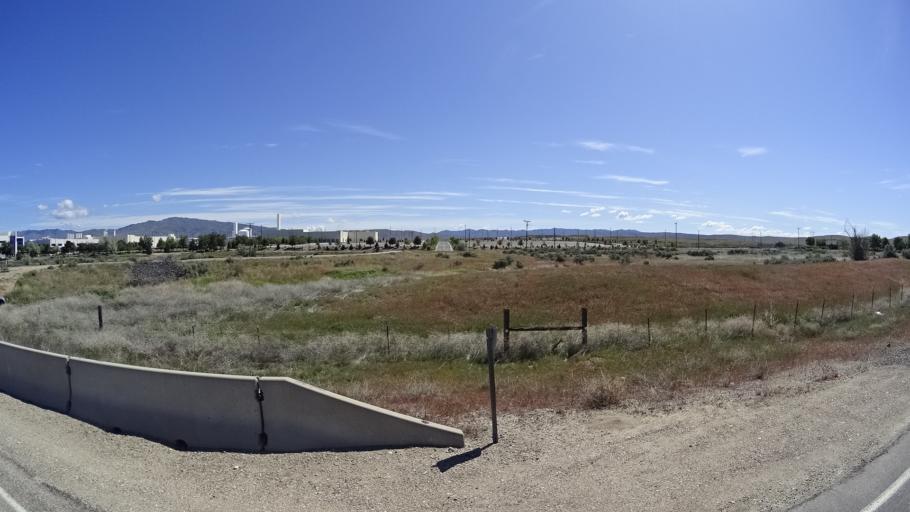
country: US
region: Idaho
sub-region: Ada County
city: Boise
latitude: 43.5201
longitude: -116.1465
